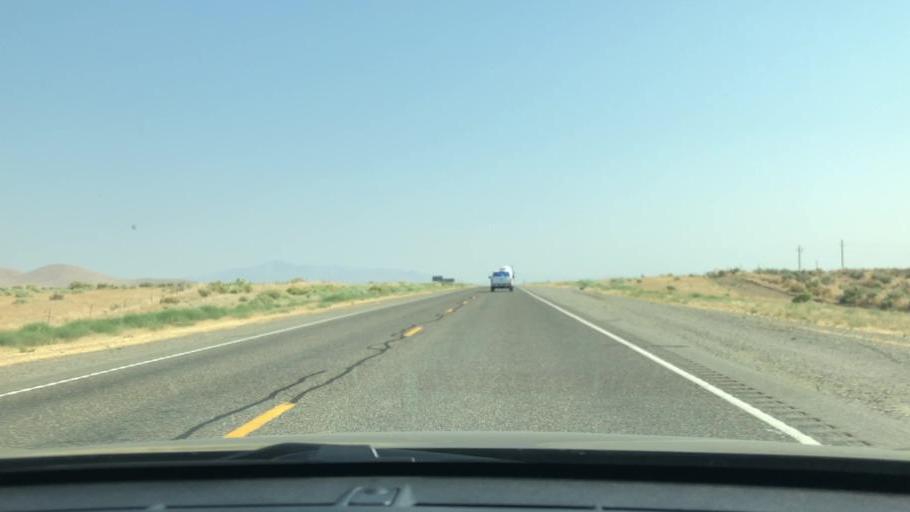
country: US
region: Nevada
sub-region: Humboldt County
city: Winnemucca
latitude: 41.1473
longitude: -117.6880
